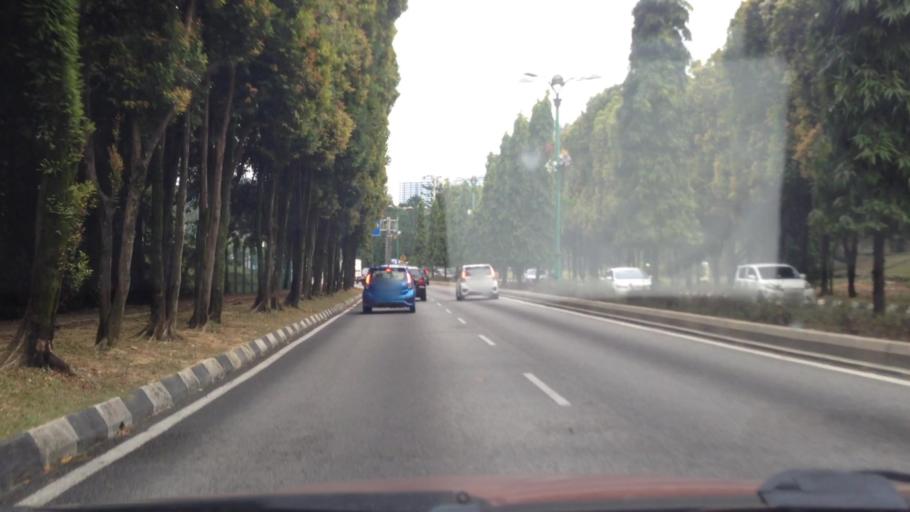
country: MY
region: Selangor
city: Shah Alam
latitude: 3.0761
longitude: 101.5348
